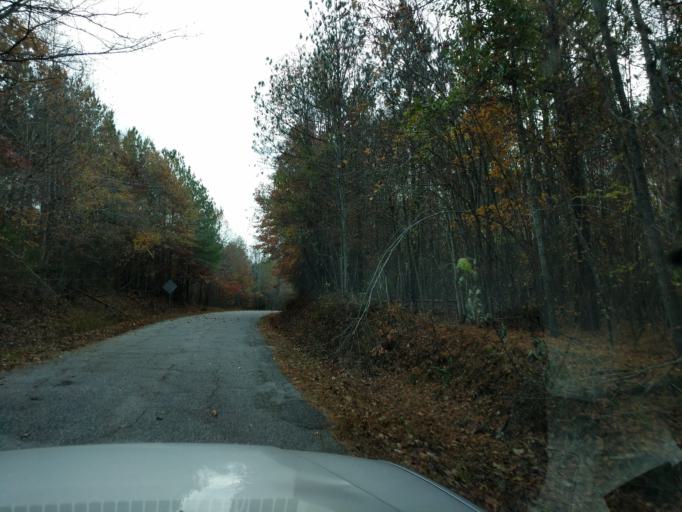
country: US
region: South Carolina
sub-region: Laurens County
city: Watts Mills
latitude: 34.5448
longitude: -81.9417
